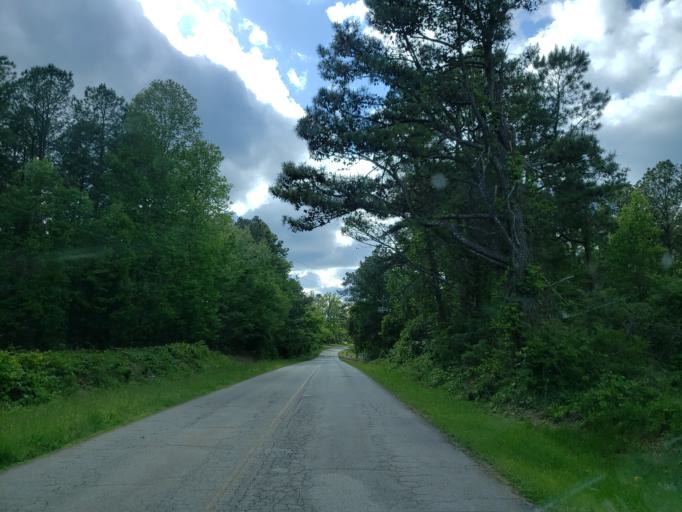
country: US
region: Georgia
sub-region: Haralson County
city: Tallapoosa
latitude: 33.6677
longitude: -85.2857
